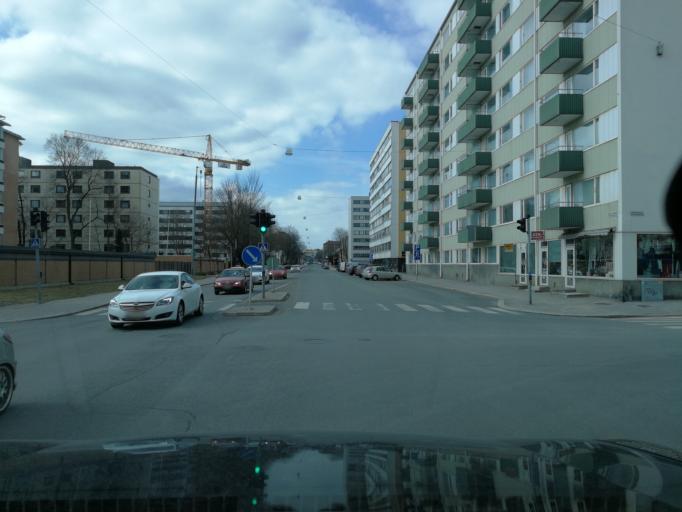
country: FI
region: Varsinais-Suomi
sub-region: Turku
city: Turku
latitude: 60.4426
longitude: 22.2717
